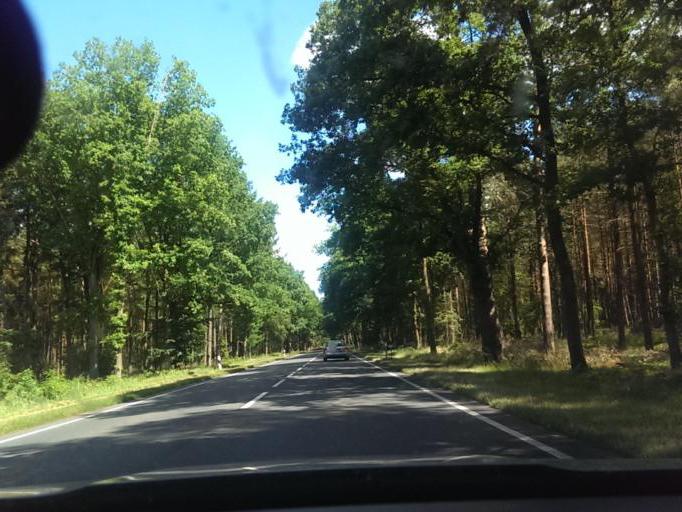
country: DE
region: Lower Saxony
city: Kirchlinteln
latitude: 52.9920
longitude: 9.2658
